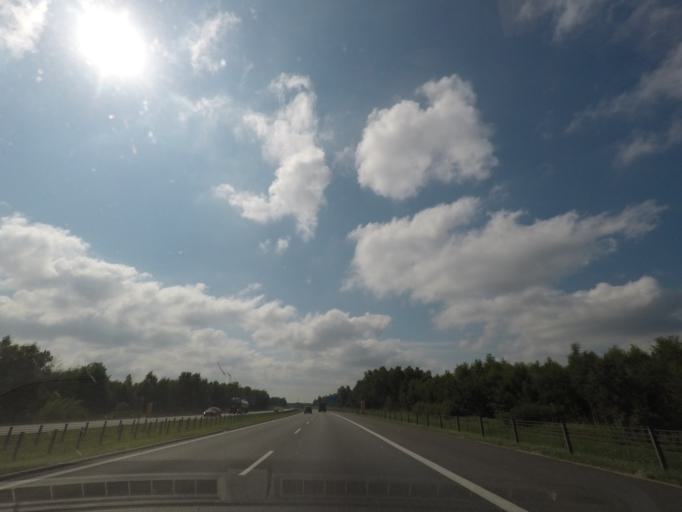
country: PL
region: Kujawsko-Pomorskie
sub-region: Powiat torunski
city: Lubicz Dolny
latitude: 53.0269
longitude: 18.7319
